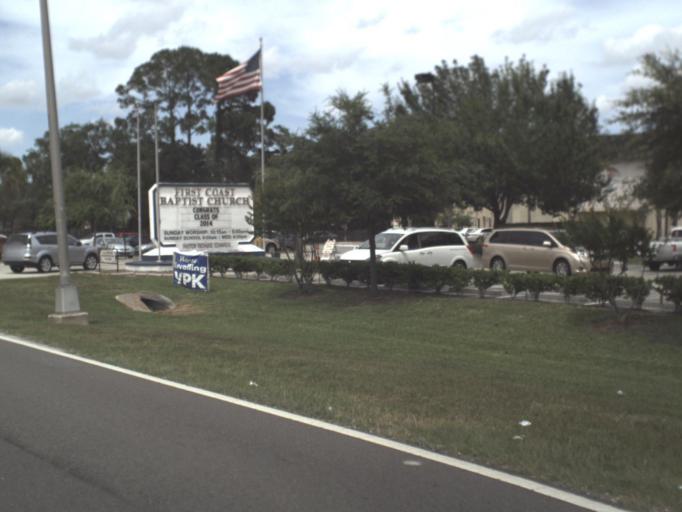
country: US
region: Florida
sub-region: Clay County
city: Bellair-Meadowbrook Terrace
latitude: 30.2096
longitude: -81.7382
